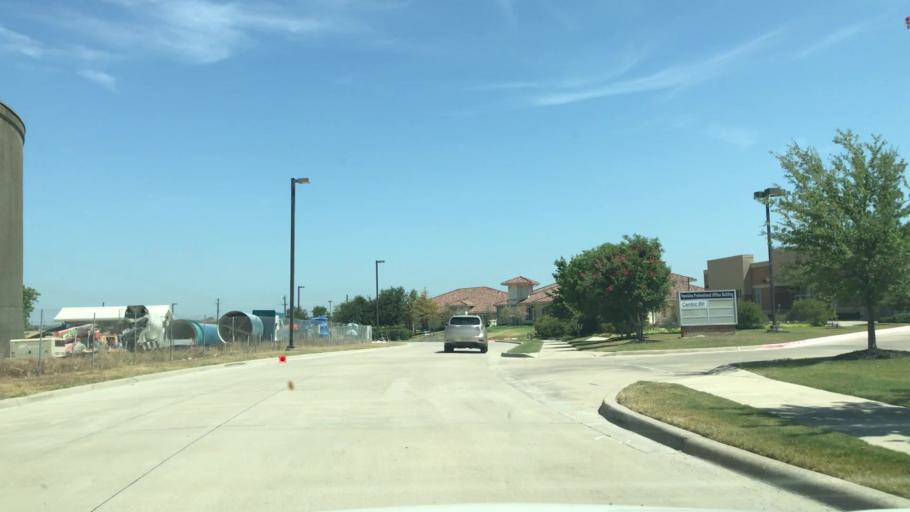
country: US
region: Texas
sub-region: Collin County
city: Allen
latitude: 33.1137
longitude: -96.6781
